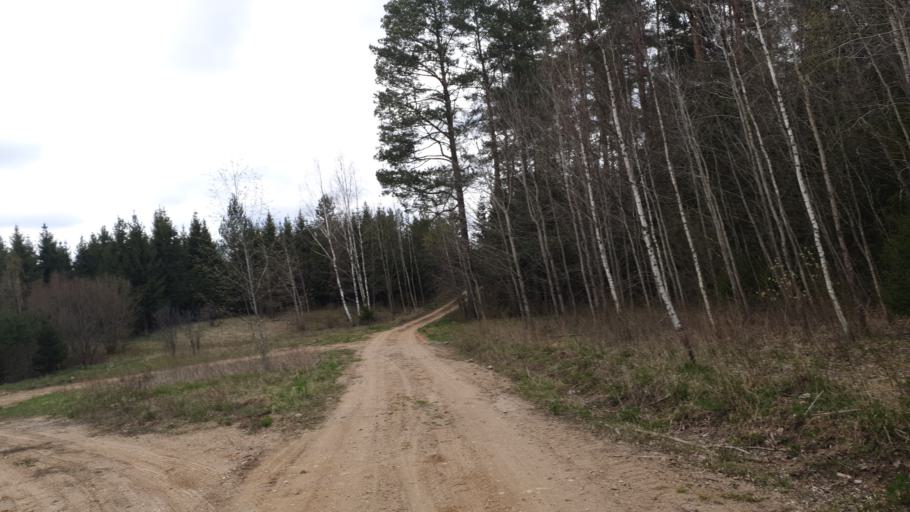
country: LT
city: Aukstadvaris
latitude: 54.5120
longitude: 24.6398
